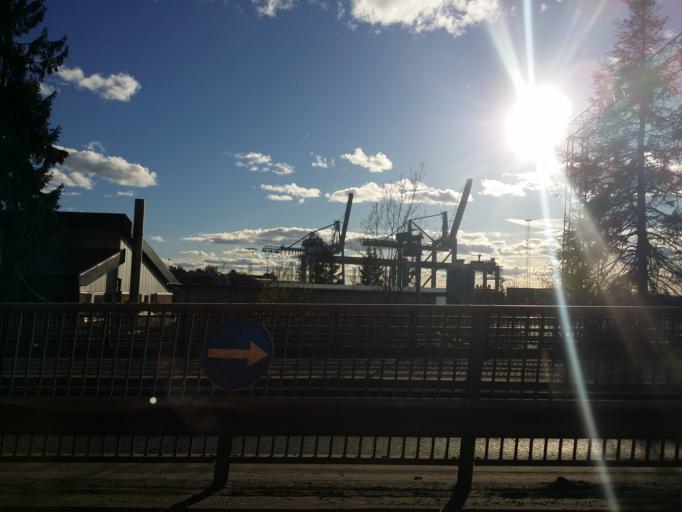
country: NO
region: Oslo
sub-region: Oslo
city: Oslo
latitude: 59.8833
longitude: 10.7701
